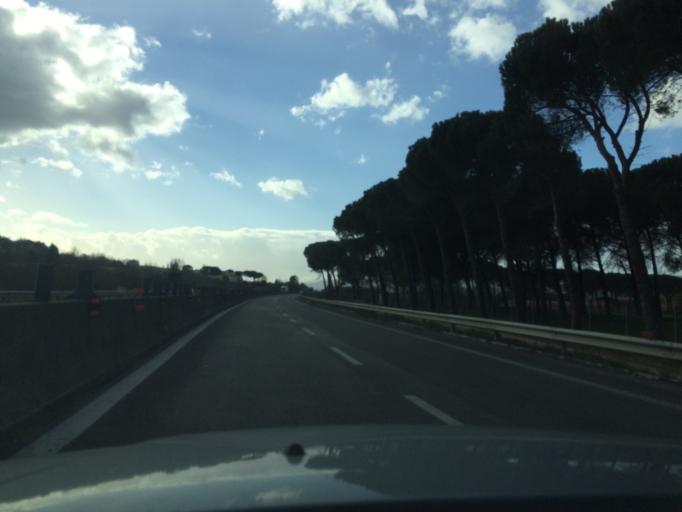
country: IT
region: Umbria
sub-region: Provincia di Perugia
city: Collepepe
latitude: 42.9096
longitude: 12.3920
